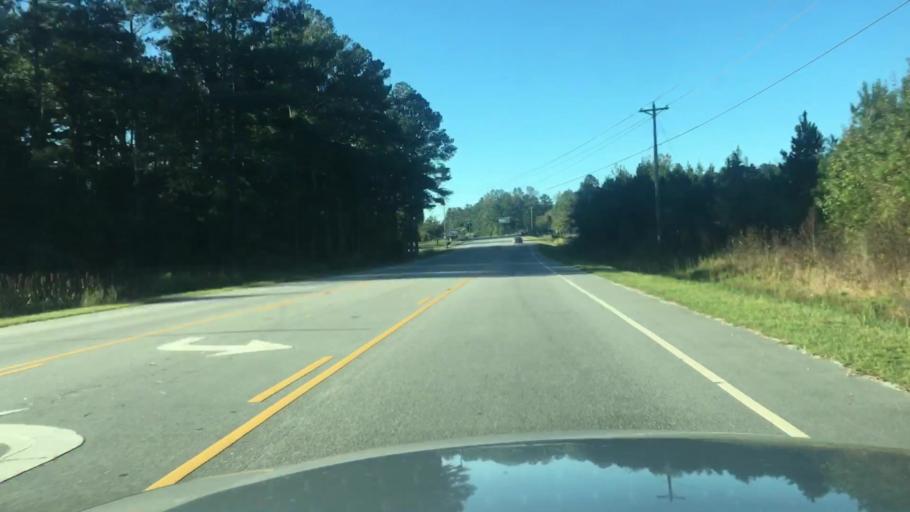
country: US
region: North Carolina
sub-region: Cumberland County
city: Spring Lake
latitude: 35.2547
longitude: -78.9262
